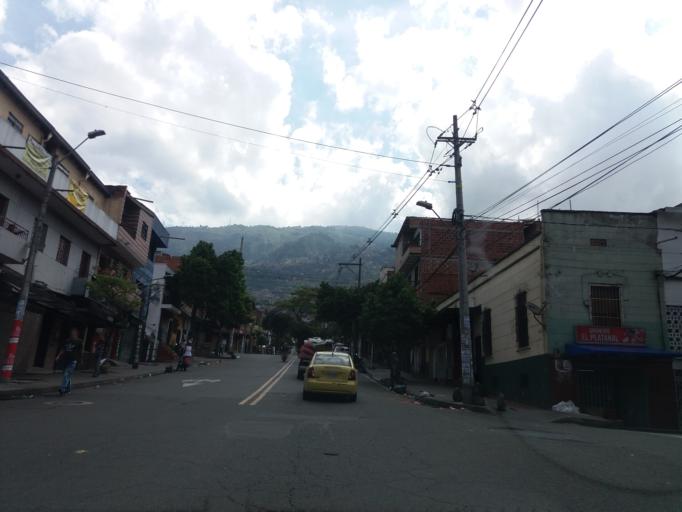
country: CO
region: Antioquia
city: Medellin
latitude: 6.2834
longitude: -75.5581
